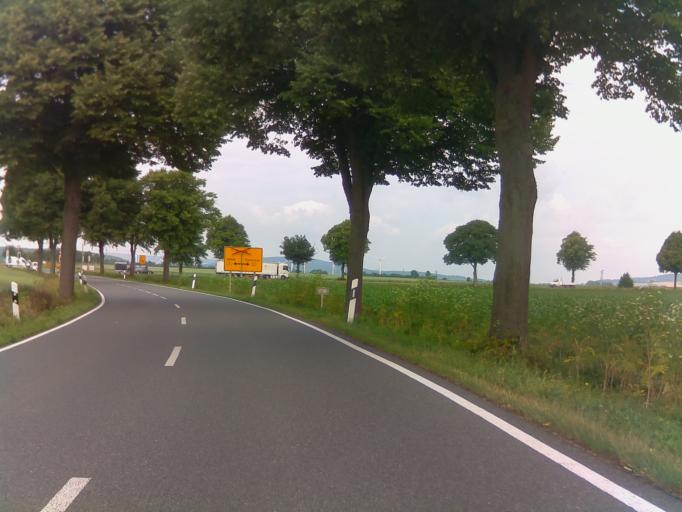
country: DE
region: Lower Saxony
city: Pattensen
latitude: 52.2093
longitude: 9.7497
